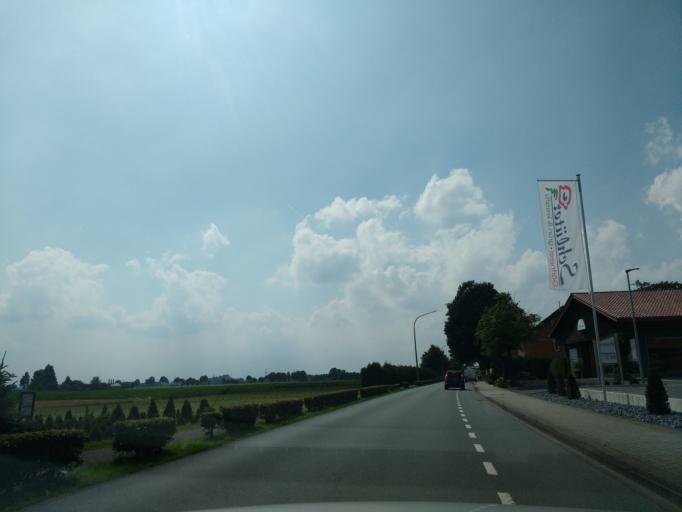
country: DE
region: North Rhine-Westphalia
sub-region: Regierungsbezirk Detmold
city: Salzkotten
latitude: 51.7119
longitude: 8.6407
